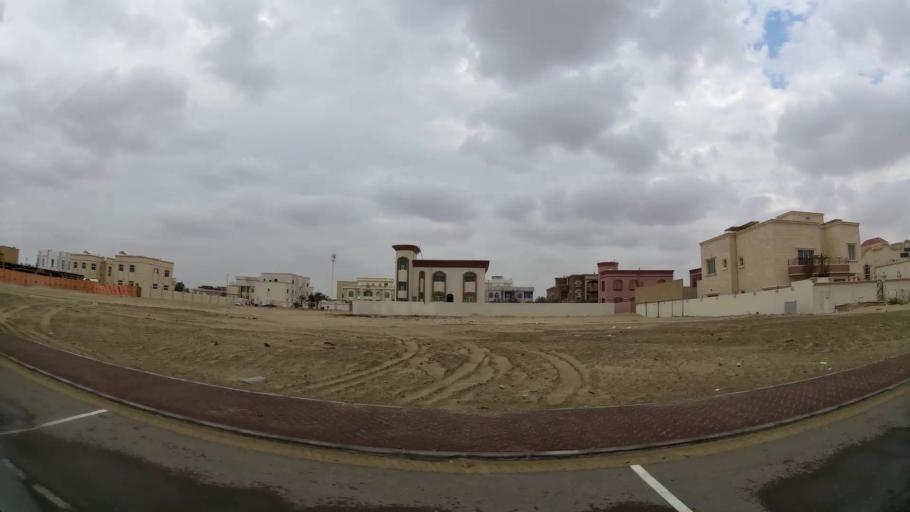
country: AE
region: Abu Dhabi
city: Abu Dhabi
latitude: 24.3458
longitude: 54.6300
